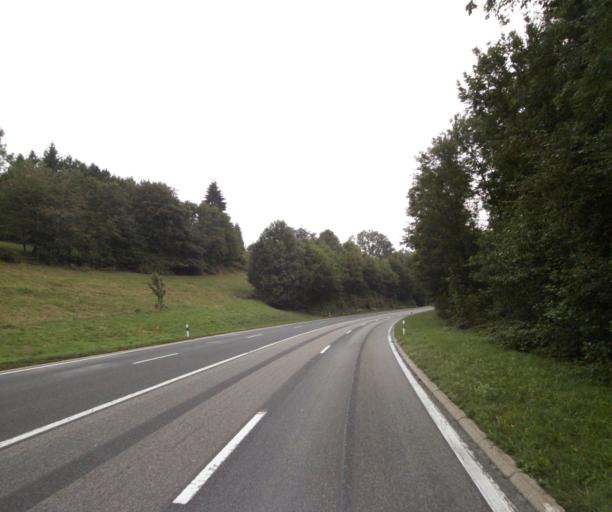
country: CH
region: Vaud
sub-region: Lausanne District
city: Epalinges
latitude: 46.5496
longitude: 6.6663
